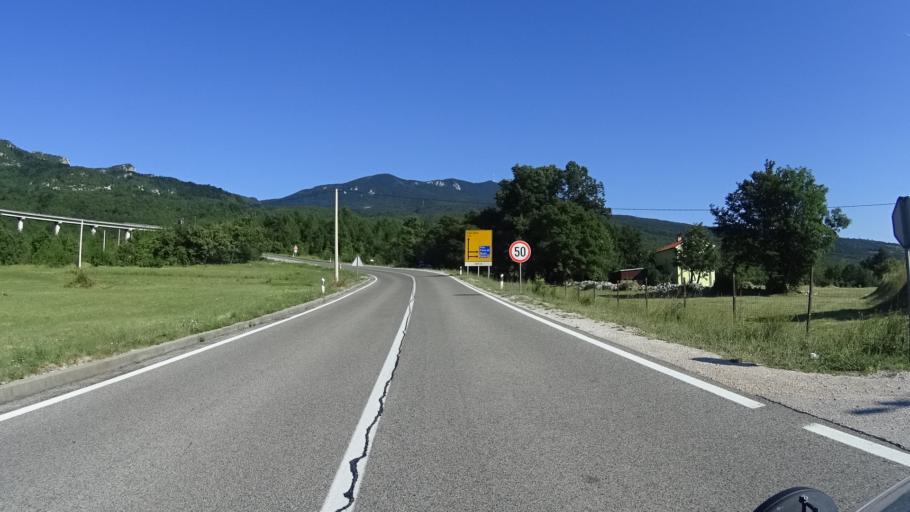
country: HR
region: Istarska
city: Lovran
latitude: 45.3209
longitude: 14.1669
